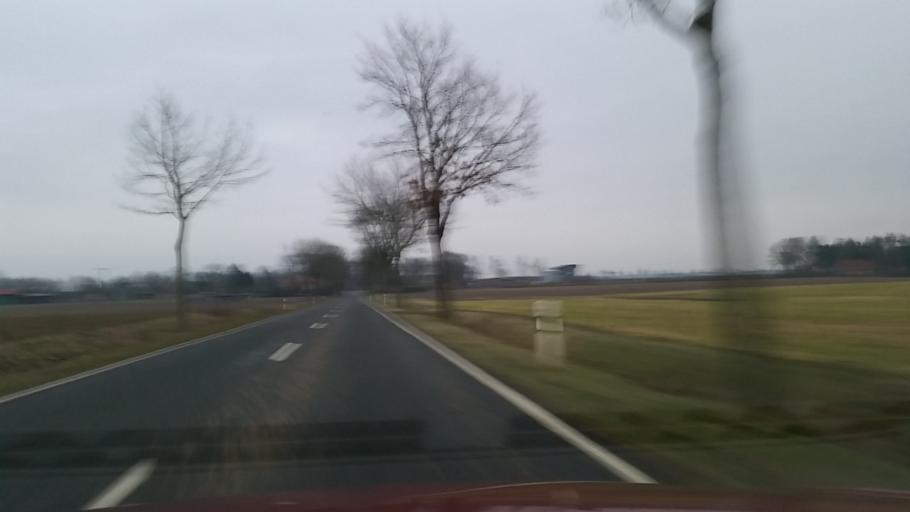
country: DE
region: Lower Saxony
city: Sprakensehl
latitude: 52.7553
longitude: 10.5106
